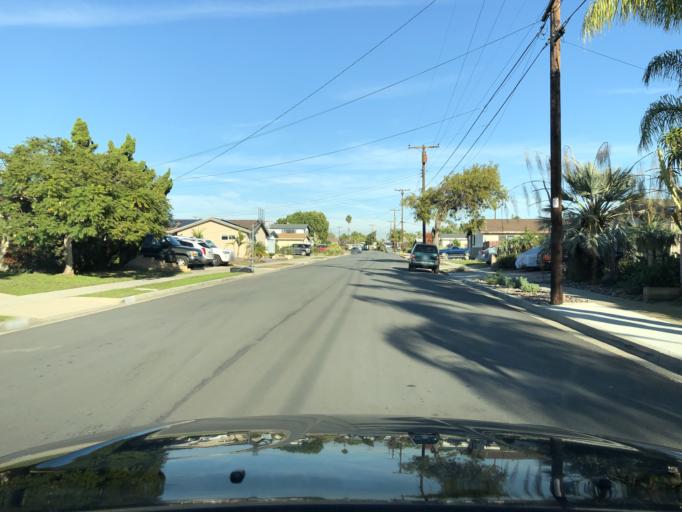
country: US
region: California
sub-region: San Diego County
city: La Jolla
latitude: 32.8183
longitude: -117.1984
